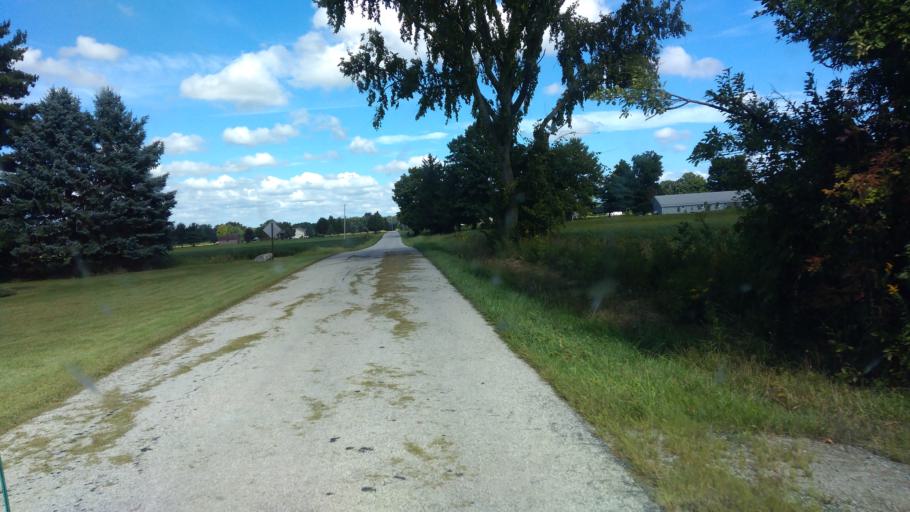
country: US
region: Ohio
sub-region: Huron County
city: Plymouth
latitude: 41.0246
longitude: -82.6517
